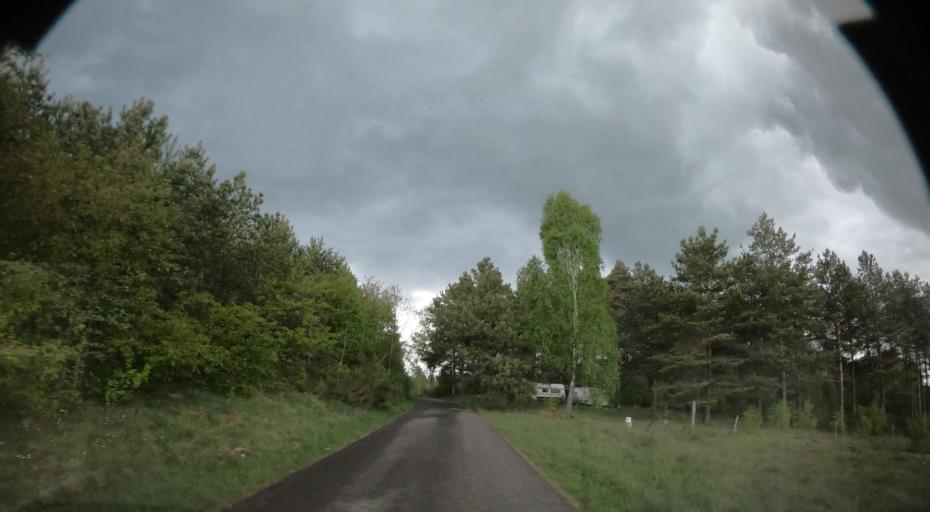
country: PL
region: West Pomeranian Voivodeship
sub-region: Powiat koszalinski
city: Polanow
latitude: 54.1178
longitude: 16.5014
